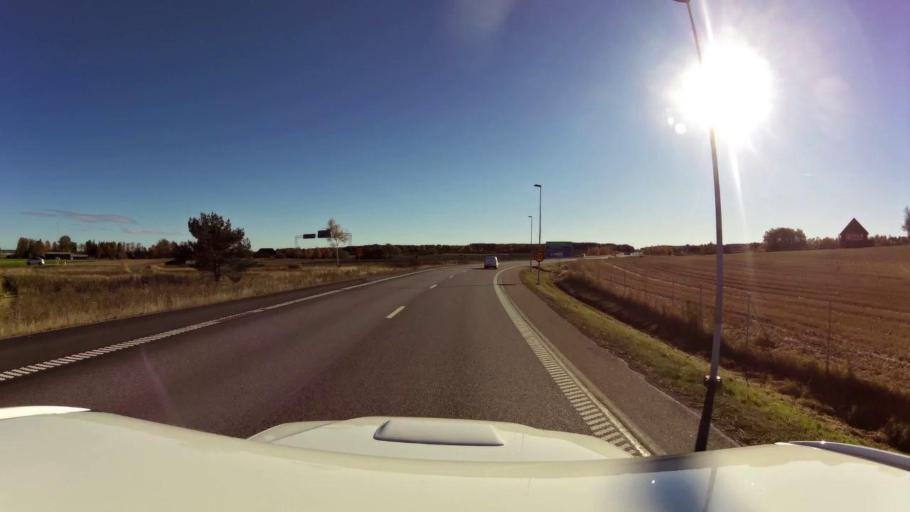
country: SE
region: OEstergoetland
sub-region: Linkopings Kommun
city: Malmslatt
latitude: 58.4318
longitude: 15.5321
